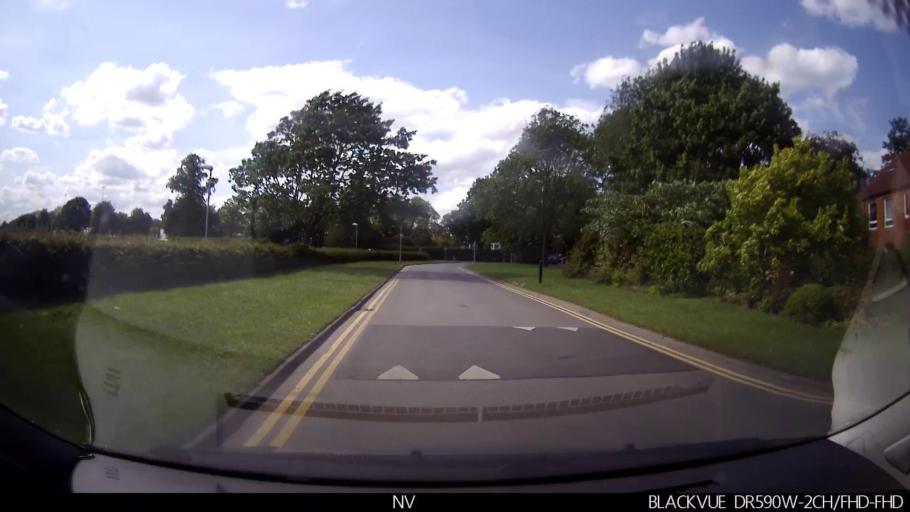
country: GB
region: England
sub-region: City of York
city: Heslington
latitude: 53.9429
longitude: -1.0508
